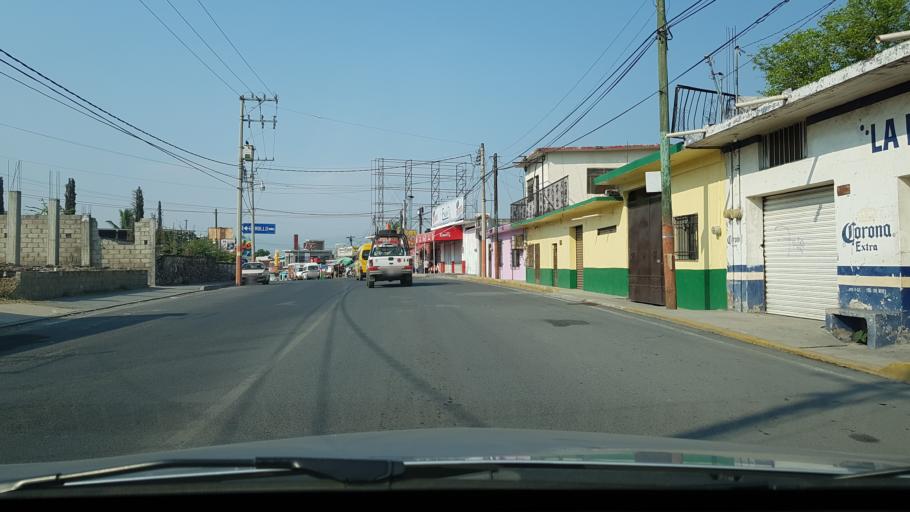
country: MX
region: Morelos
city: Tlaquiltenango
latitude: 18.6387
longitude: -99.1602
